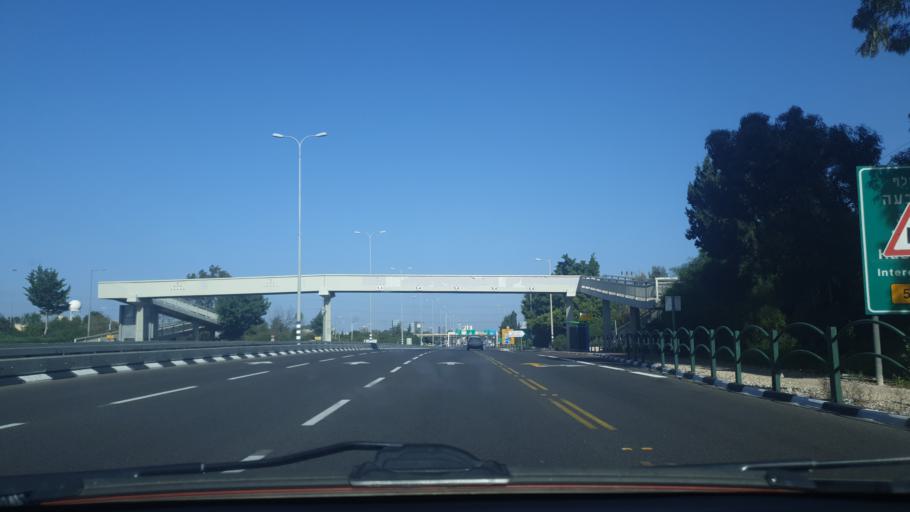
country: IL
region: Central District
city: Bet Dagan
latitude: 32.0054
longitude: 34.8181
